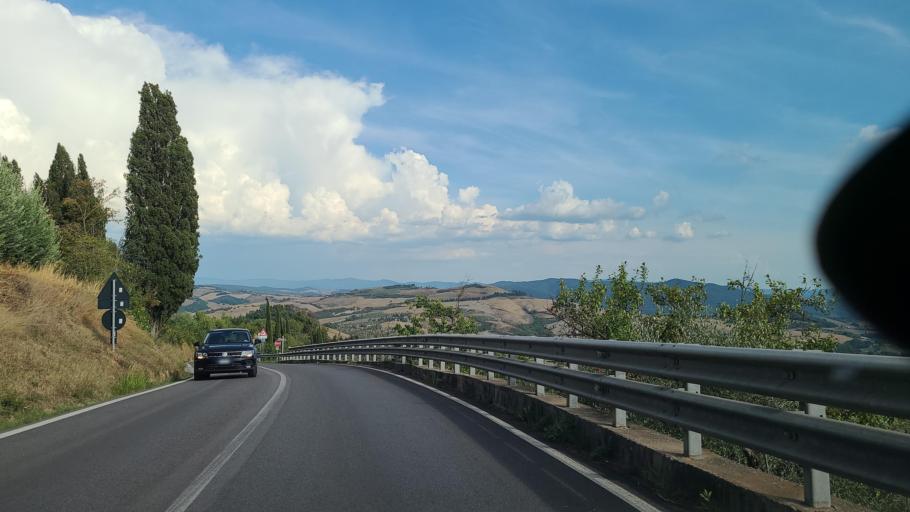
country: IT
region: Tuscany
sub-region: Province of Pisa
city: Volterra
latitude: 43.3972
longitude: 10.8761
